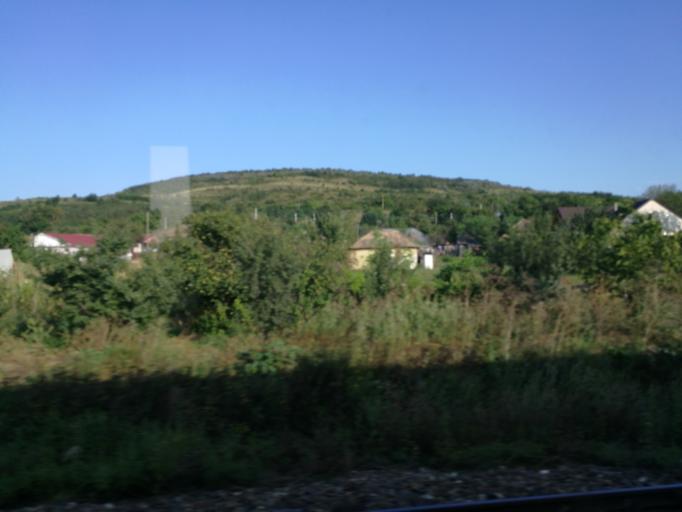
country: RO
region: Vaslui
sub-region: Comuna Banca
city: Banca
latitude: 46.3404
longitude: 27.7938
